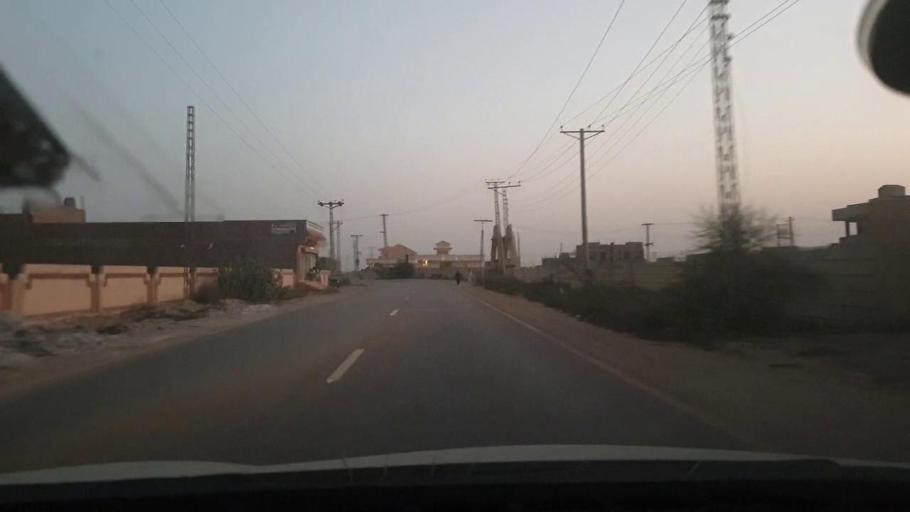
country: PK
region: Sindh
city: Tando Adam
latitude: 25.7488
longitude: 68.6448
